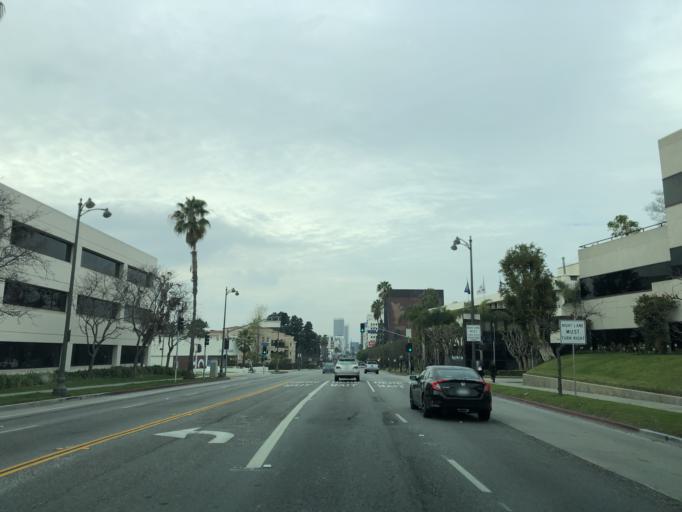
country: US
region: California
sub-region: Los Angeles County
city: Hollywood
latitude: 34.0621
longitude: -118.3340
